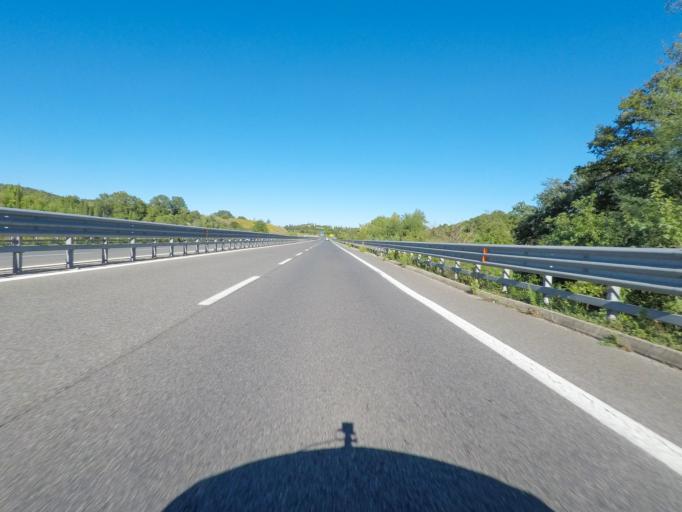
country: IT
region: Tuscany
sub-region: Provincia di Grosseto
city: Campagnatico
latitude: 42.9102
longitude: 11.2510
